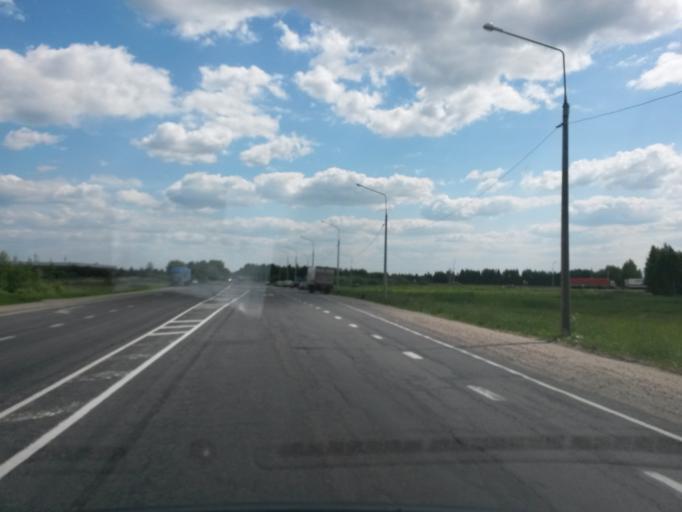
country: RU
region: Jaroslavl
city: Yaroslavl
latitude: 57.5513
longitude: 39.8875
